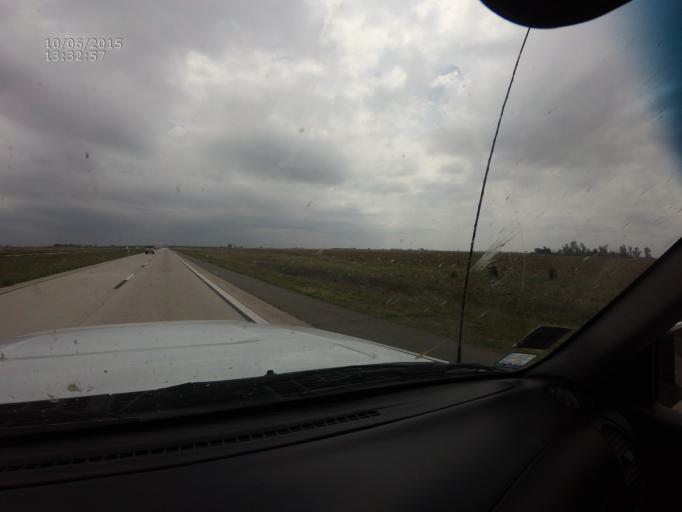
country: AR
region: Cordoba
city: Leones
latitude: -32.6251
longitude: -62.3179
